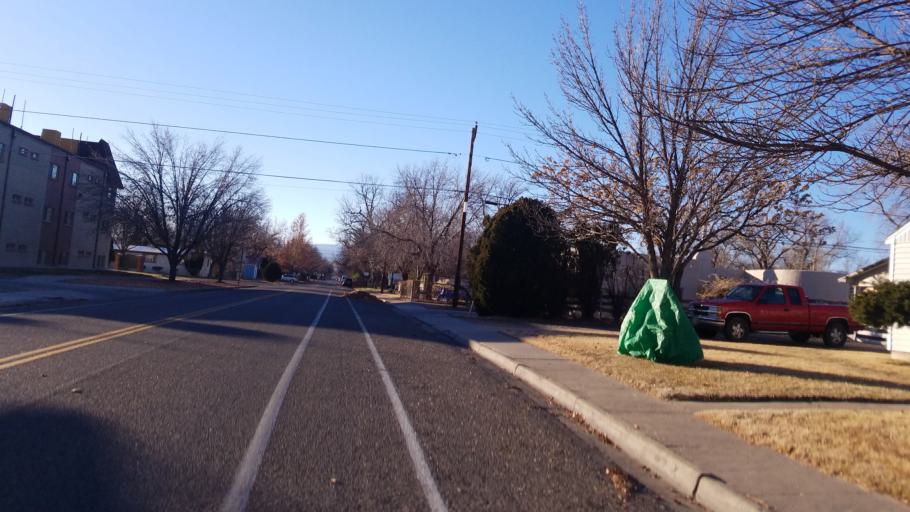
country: US
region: Colorado
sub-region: Mesa County
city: Grand Junction
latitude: 39.0762
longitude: -108.5560
